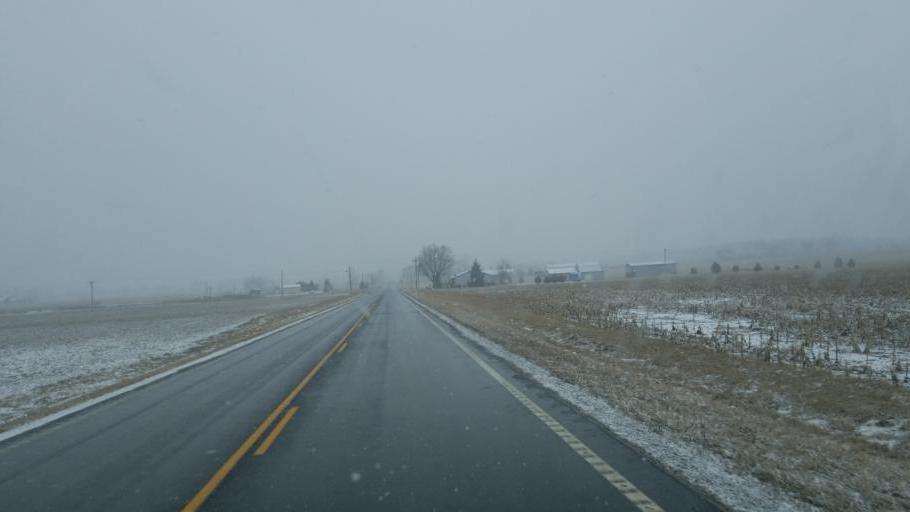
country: US
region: Ohio
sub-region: Defiance County
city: Hicksville
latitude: 41.3231
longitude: -84.7476
